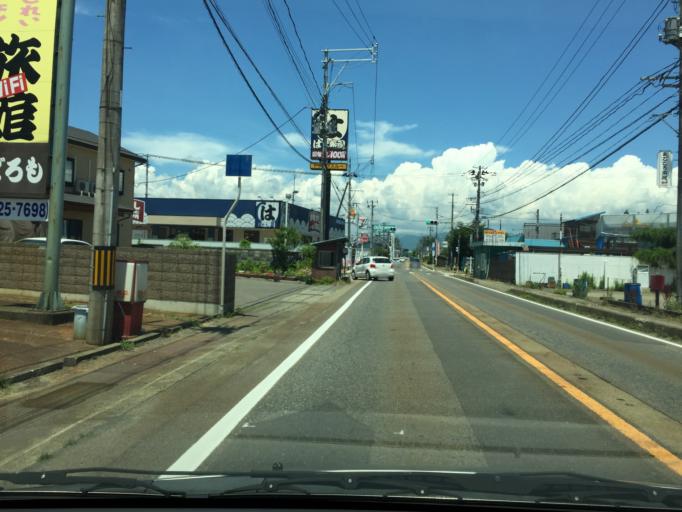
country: JP
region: Fukushima
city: Kitakata
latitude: 37.6308
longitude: 139.8915
